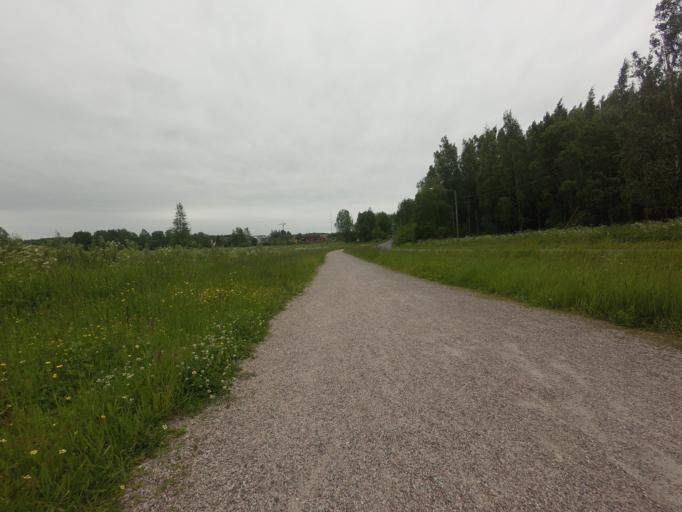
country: FI
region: Uusimaa
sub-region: Helsinki
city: Kauniainen
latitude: 60.1870
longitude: 24.7291
